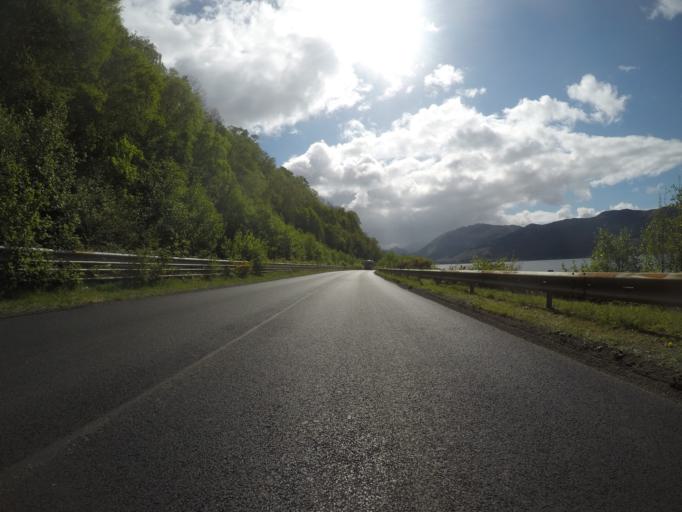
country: GB
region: Scotland
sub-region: Highland
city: Fort William
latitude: 57.2538
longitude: -5.4765
